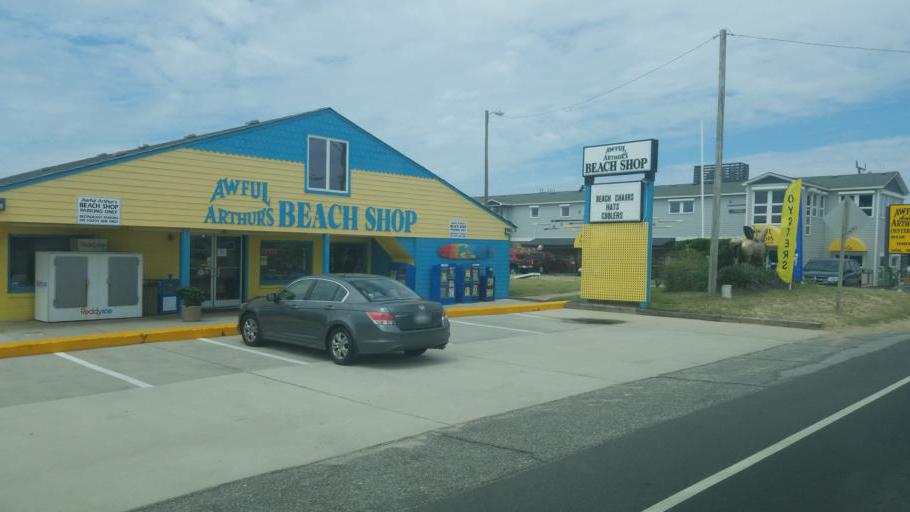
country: US
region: North Carolina
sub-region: Dare County
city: Kill Devil Hills
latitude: 36.0433
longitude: -75.6750
